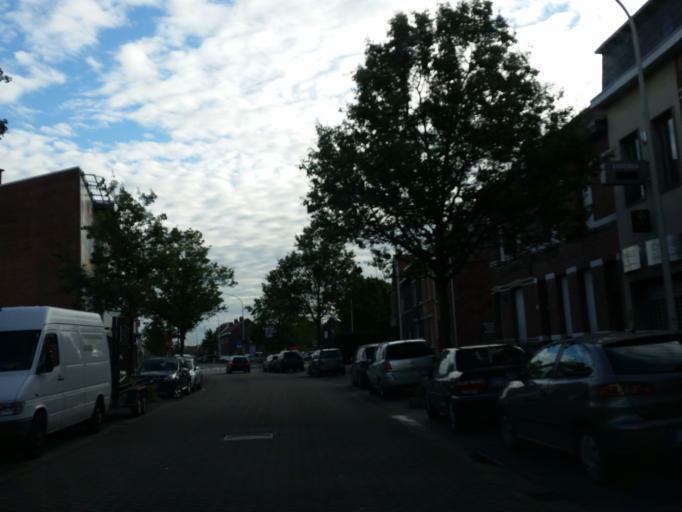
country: BE
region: Flanders
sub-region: Provincie Antwerpen
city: Kapellen
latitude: 51.2802
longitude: 4.4200
